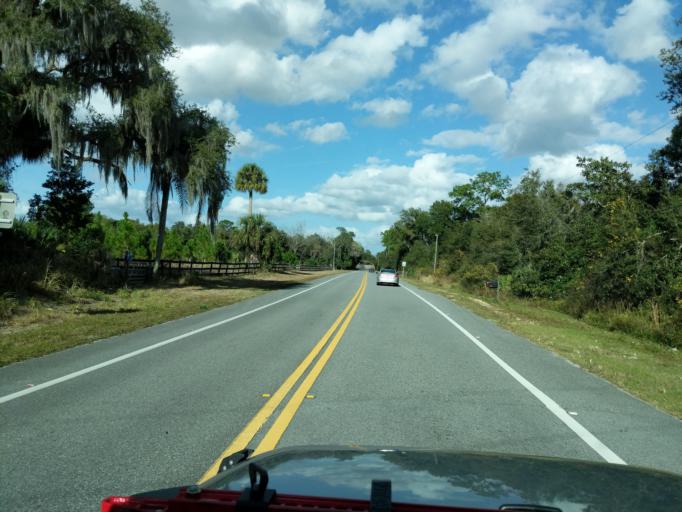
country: US
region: Florida
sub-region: Seminole County
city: Geneva
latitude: 28.7159
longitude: -81.1176
